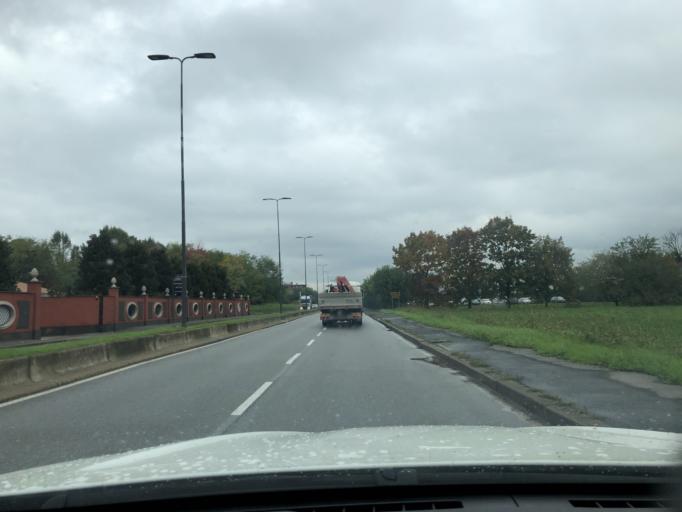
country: IT
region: Lombardy
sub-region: Citta metropolitana di Milano
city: Settimo Milanese
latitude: 45.4589
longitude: 9.0691
